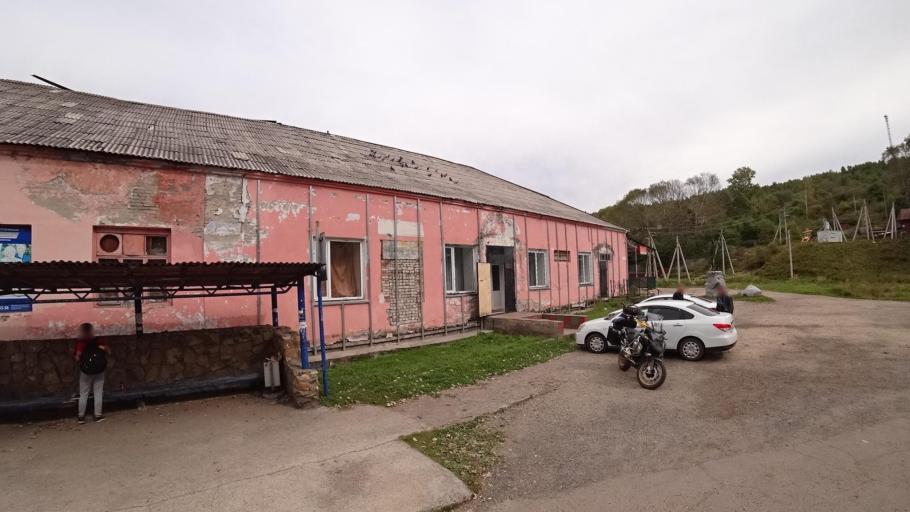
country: RU
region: Jewish Autonomous Oblast
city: Khingansk
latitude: 49.0195
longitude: 131.0629
